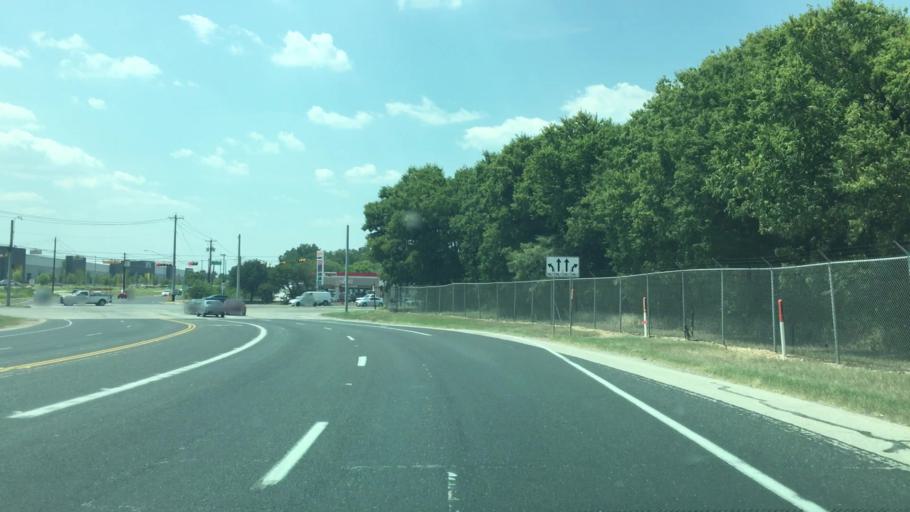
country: US
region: Texas
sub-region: Travis County
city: Austin
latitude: 30.1824
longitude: -97.6867
